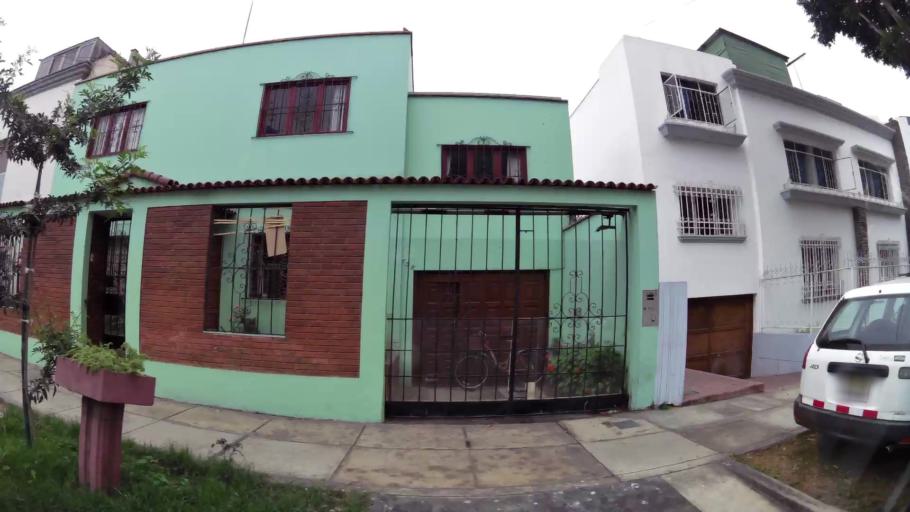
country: PE
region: Lima
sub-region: Lima
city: Surco
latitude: -12.1296
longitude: -77.0209
